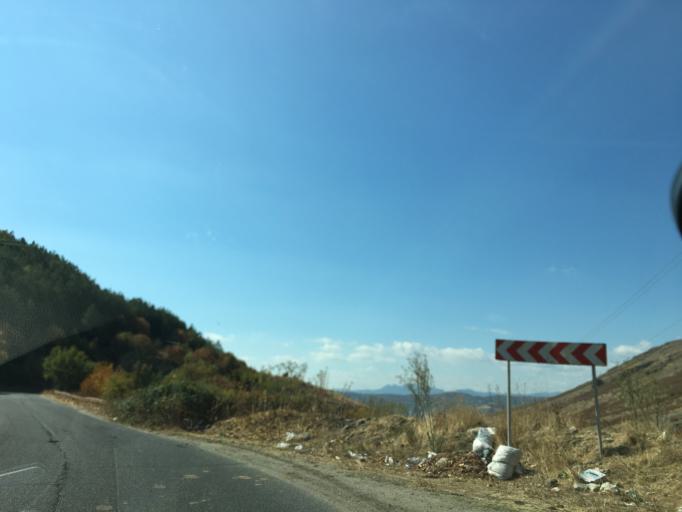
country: BG
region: Kurdzhali
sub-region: Obshtina Kurdzhali
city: Kurdzhali
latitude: 41.5263
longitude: 25.4469
